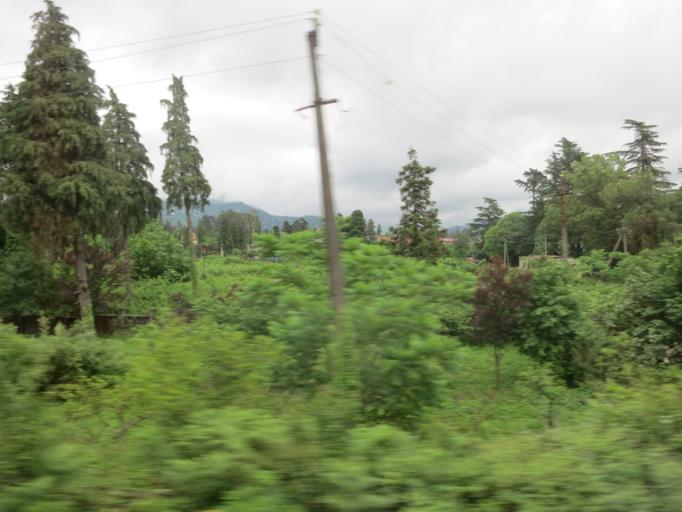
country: GE
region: Ajaria
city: Makhinjauri
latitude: 41.7197
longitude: 41.7287
